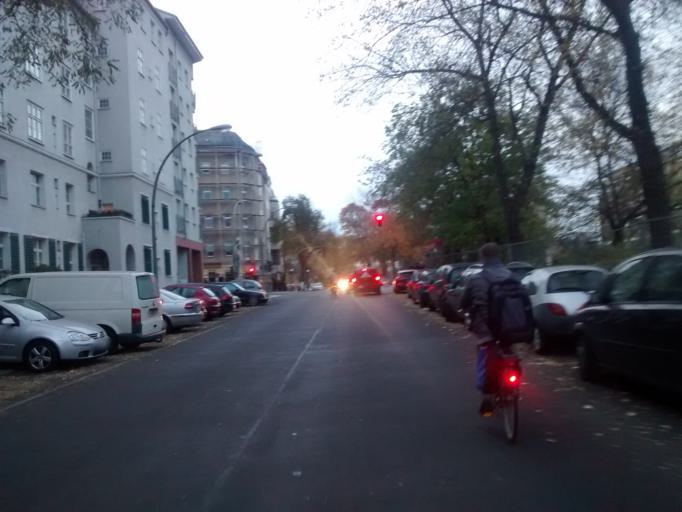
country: DE
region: Berlin
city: Moabit
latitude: 52.5188
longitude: 13.3196
